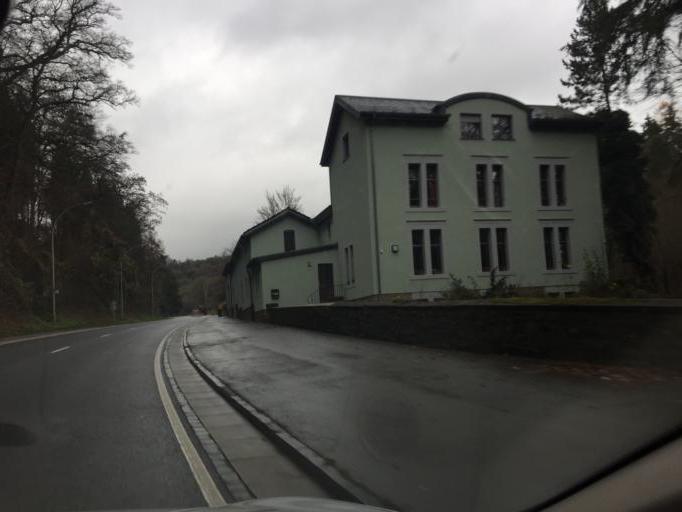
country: LU
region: Diekirch
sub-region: Canton de Diekirch
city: Diekirch
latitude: 49.8758
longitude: 6.1536
